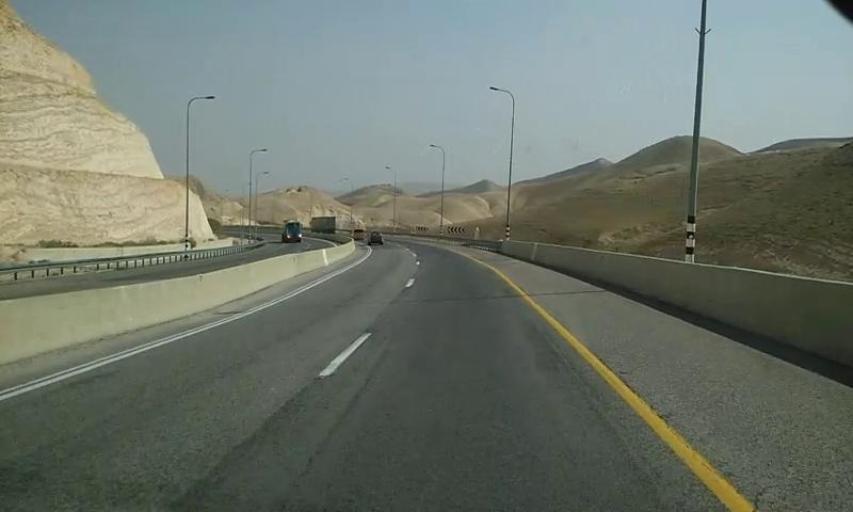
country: PS
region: West Bank
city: Jericho
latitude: 31.8090
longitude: 35.3924
